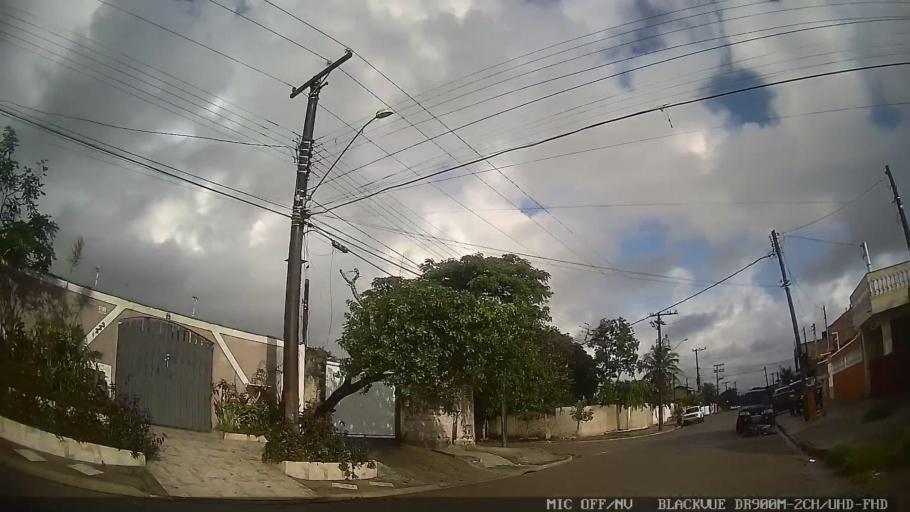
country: BR
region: Sao Paulo
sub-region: Itanhaem
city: Itanhaem
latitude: -24.1851
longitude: -46.8581
